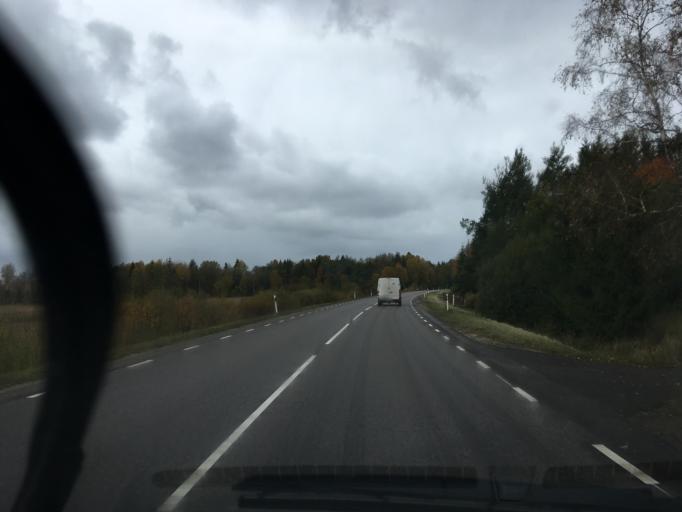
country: EE
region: Harju
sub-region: Anija vald
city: Kehra
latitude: 59.3317
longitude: 25.3150
